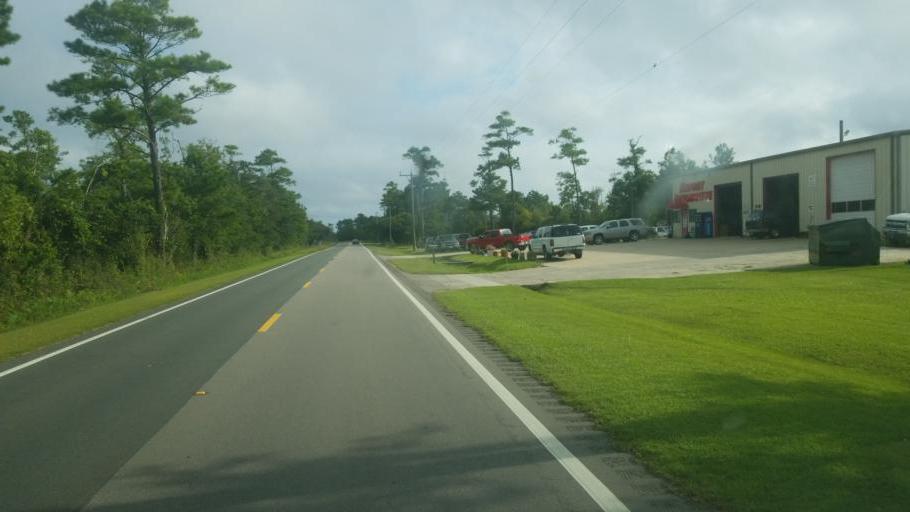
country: US
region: North Carolina
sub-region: Dare County
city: Manteo
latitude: 35.8828
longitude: -75.6592
